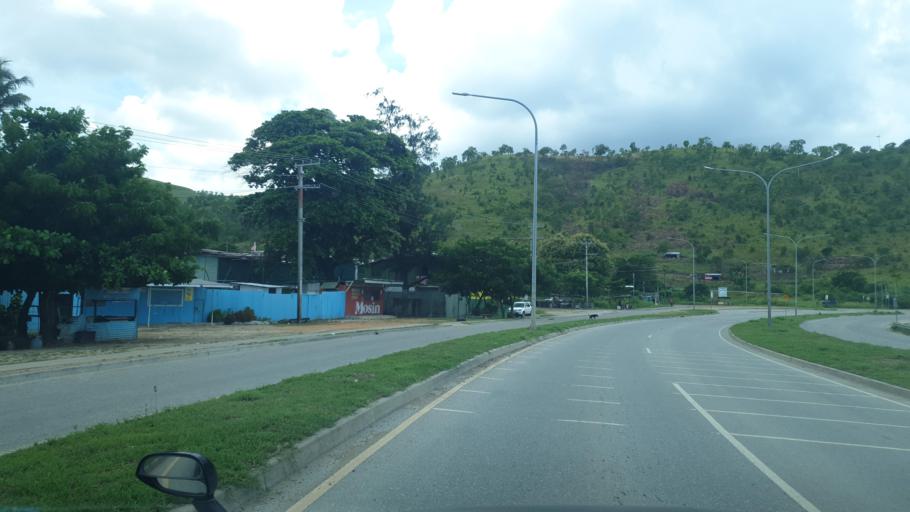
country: PG
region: National Capital
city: Port Moresby
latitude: -9.4383
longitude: 147.1391
